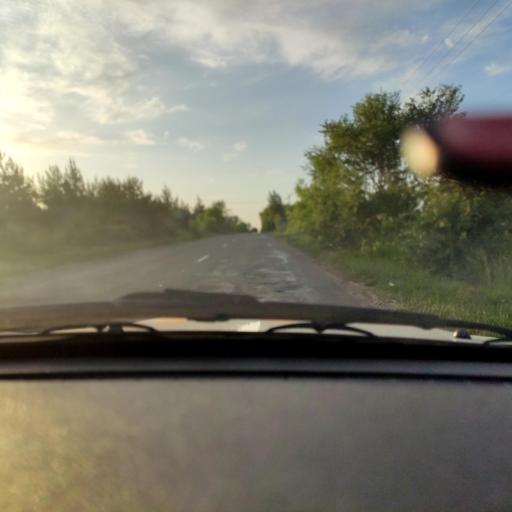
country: RU
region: Voronezj
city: Podgornoye
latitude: 51.8326
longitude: 39.2044
